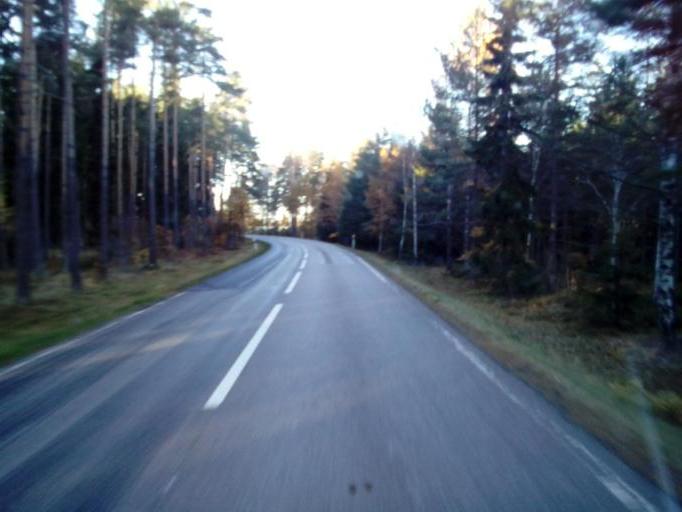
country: SE
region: OErebro
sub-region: Hallsbergs Kommun
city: Palsboda
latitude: 58.8131
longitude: 15.4143
